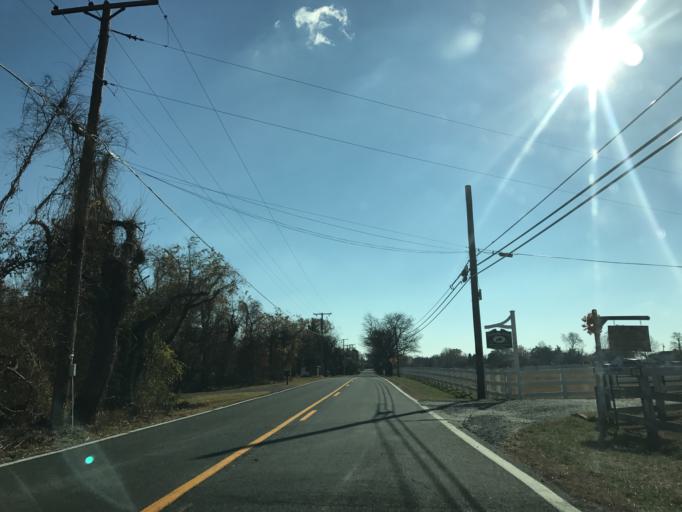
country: US
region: Maryland
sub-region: Anne Arundel County
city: Lake Shore
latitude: 39.0965
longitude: -76.4313
